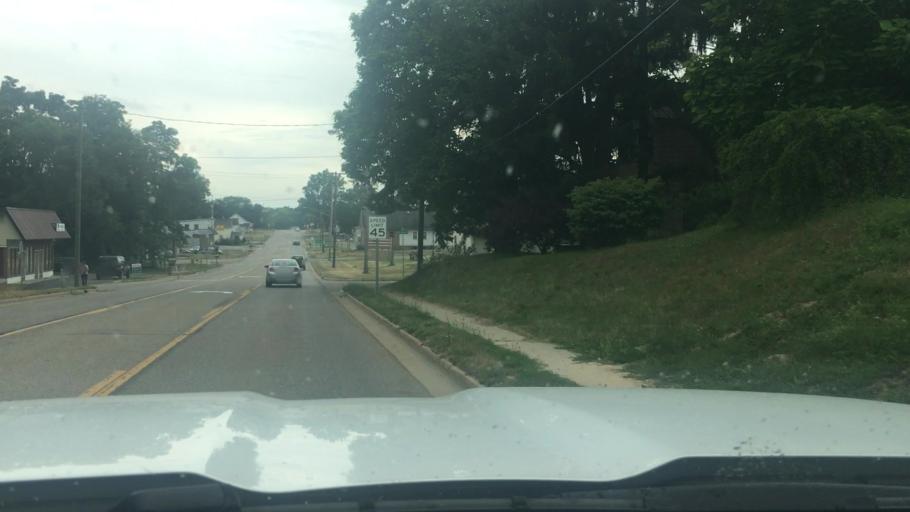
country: US
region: Michigan
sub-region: Ionia County
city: Ionia
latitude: 42.9874
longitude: -85.0796
